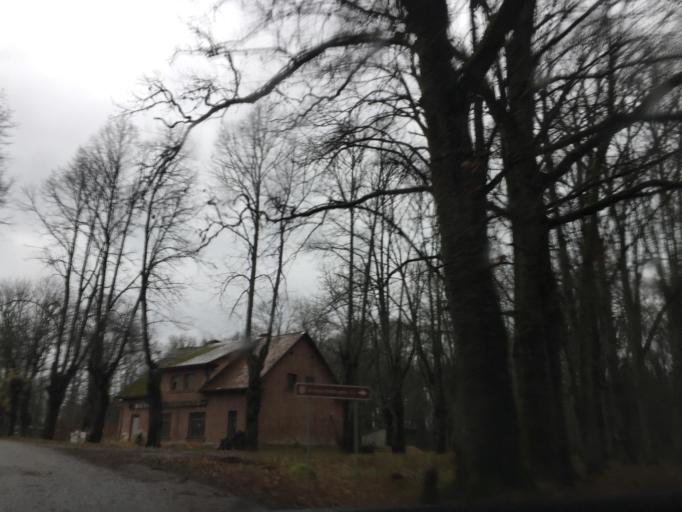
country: LV
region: Aloja
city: Aloja
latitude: 57.6603
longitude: 24.7770
